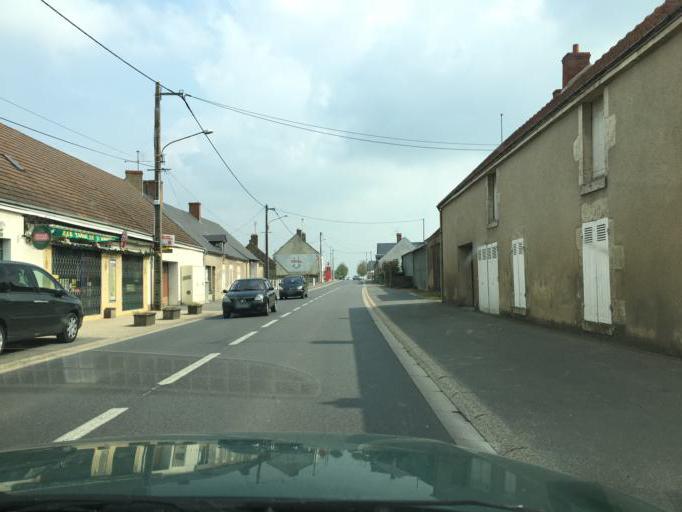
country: FR
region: Centre
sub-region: Departement du Loir-et-Cher
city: Ouzouer-le-Marche
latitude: 47.9034
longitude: 1.4643
